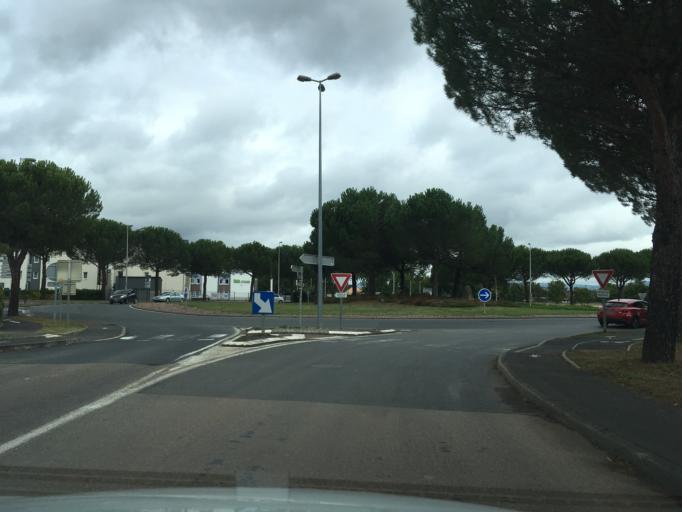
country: FR
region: Limousin
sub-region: Departement de la Correze
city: Saint-Pantaleon-de-Larche
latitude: 45.1439
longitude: 1.4758
